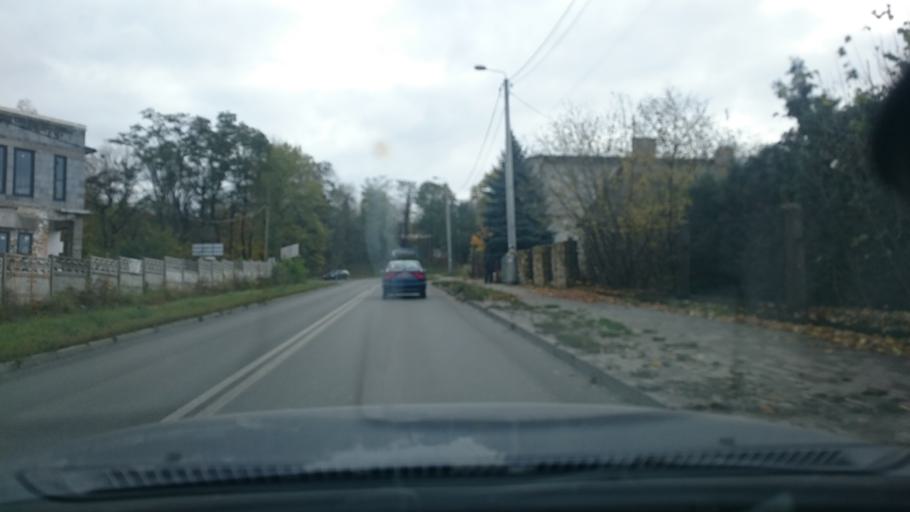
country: PL
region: Silesian Voivodeship
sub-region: Powiat bedzinski
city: Strzyzowice
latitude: 50.3516
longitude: 19.0884
